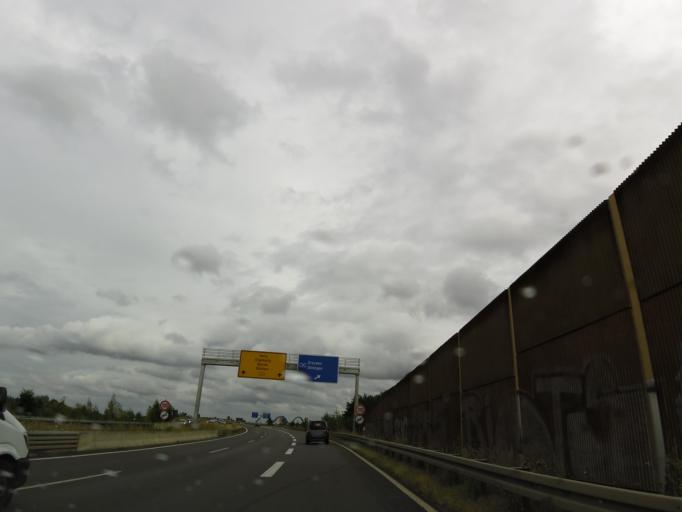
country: DE
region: Saxony
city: Markkleeberg
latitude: 51.2534
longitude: 12.3858
